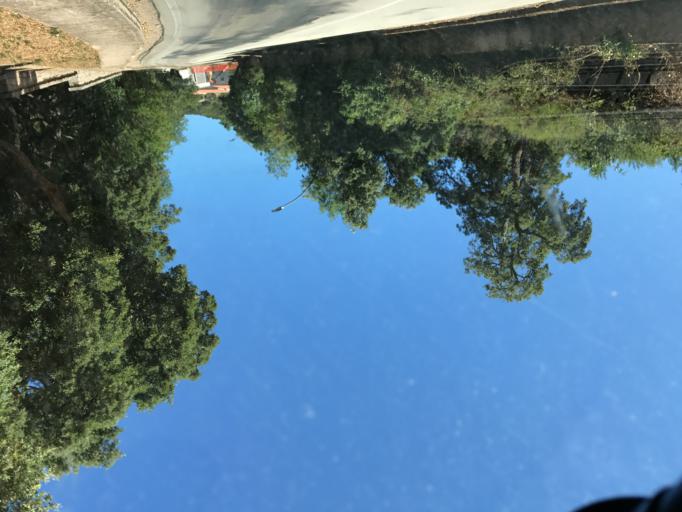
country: IT
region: Sardinia
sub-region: Provincia di Olbia-Tempio
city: Calangianus
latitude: 40.9136
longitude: 9.1984
